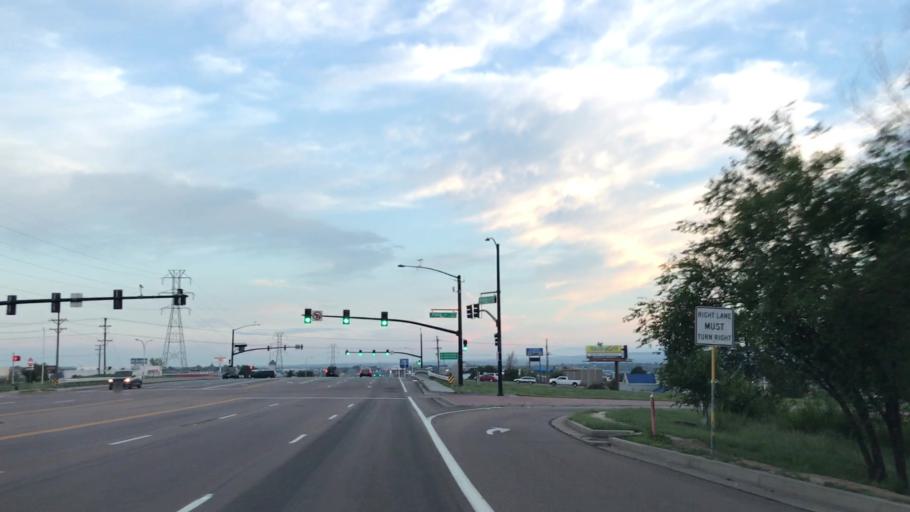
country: US
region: Colorado
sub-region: El Paso County
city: Cimarron Hills
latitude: 38.8409
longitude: -104.7576
